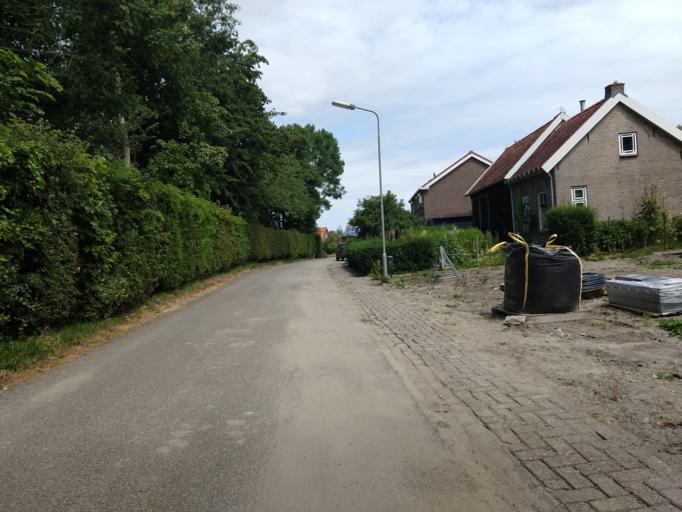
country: NL
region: Zeeland
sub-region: Gemeente Goes
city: Goes
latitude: 51.5318
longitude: 3.7997
